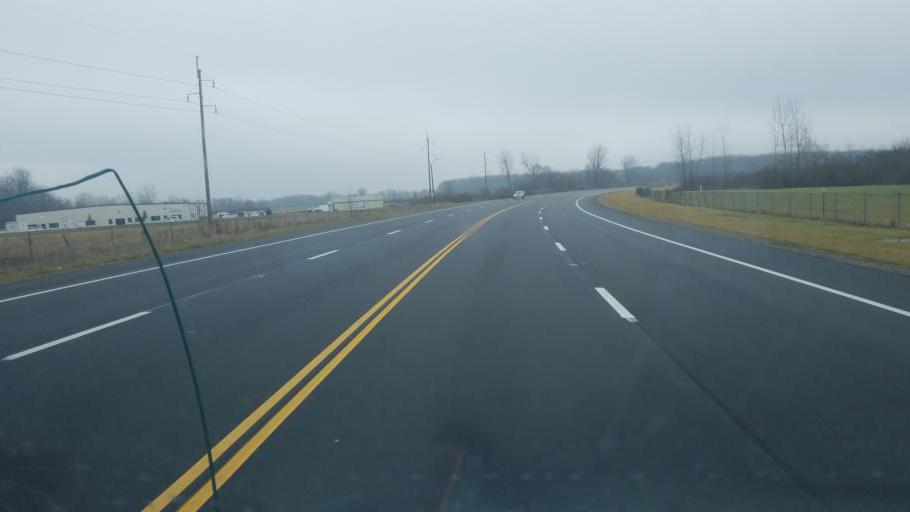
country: US
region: Ohio
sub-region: Champaign County
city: North Lewisburg
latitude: 40.3291
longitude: -83.5755
